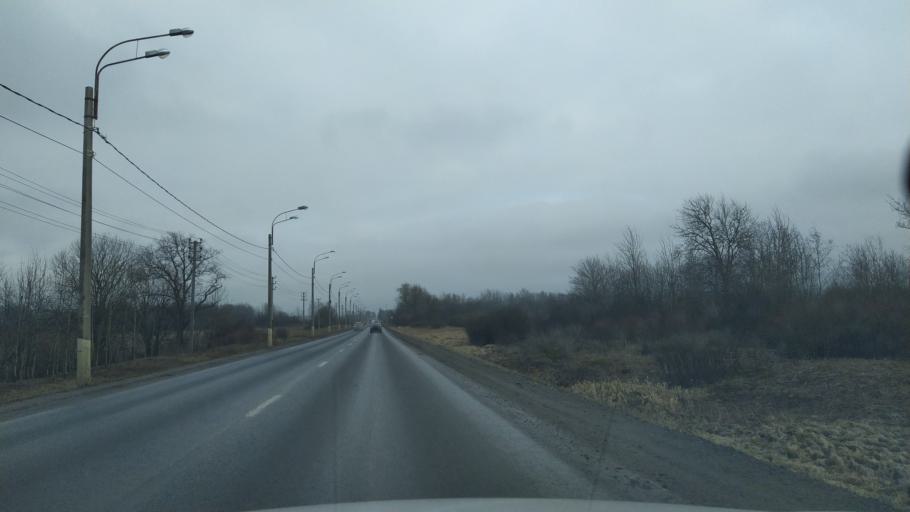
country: RU
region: St.-Petersburg
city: Aleksandrovskaya
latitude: 59.7138
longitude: 30.3031
